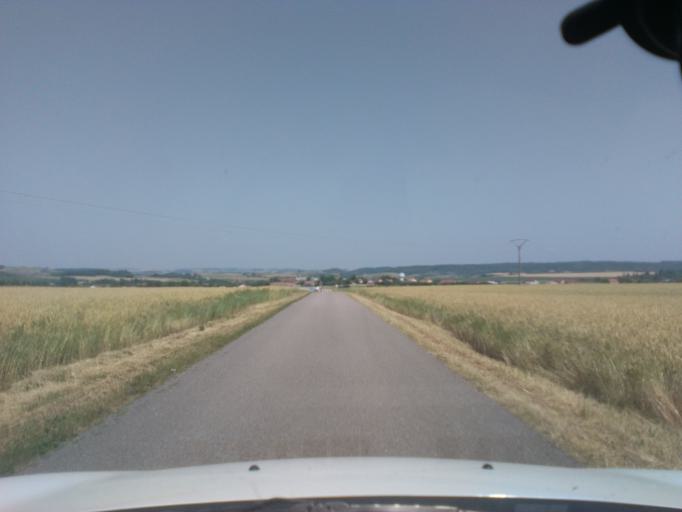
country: FR
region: Lorraine
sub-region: Departement des Vosges
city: Mirecourt
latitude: 48.3145
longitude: 6.1120
